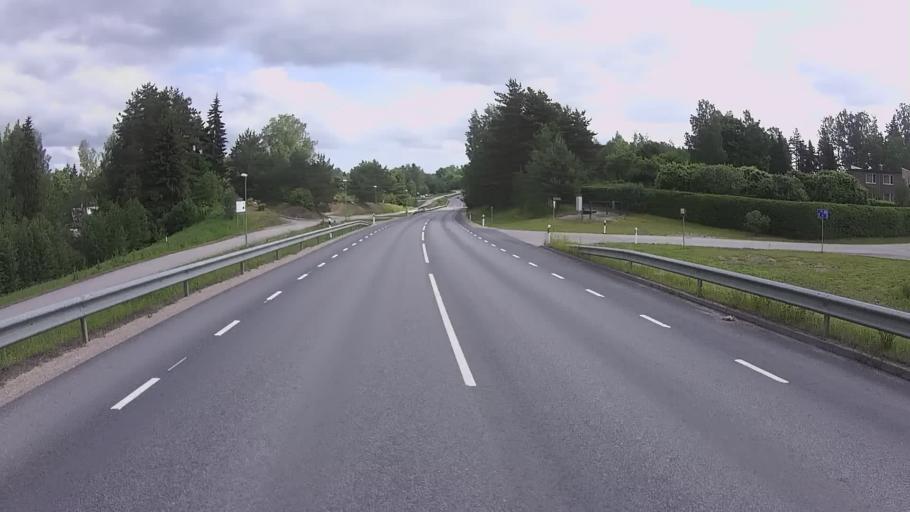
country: EE
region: Polvamaa
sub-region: Polva linn
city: Polva
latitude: 58.0663
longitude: 27.0586
